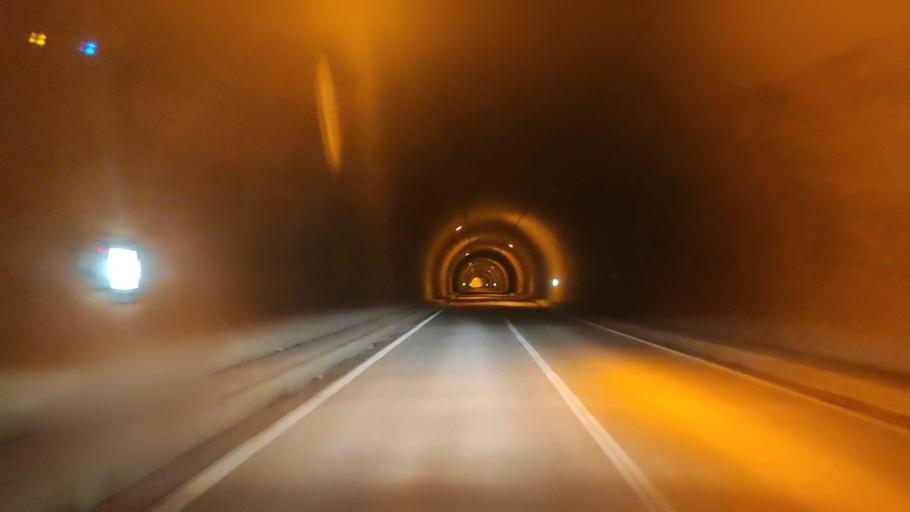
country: JP
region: Kumamoto
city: Matsubase
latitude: 32.5071
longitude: 130.9202
